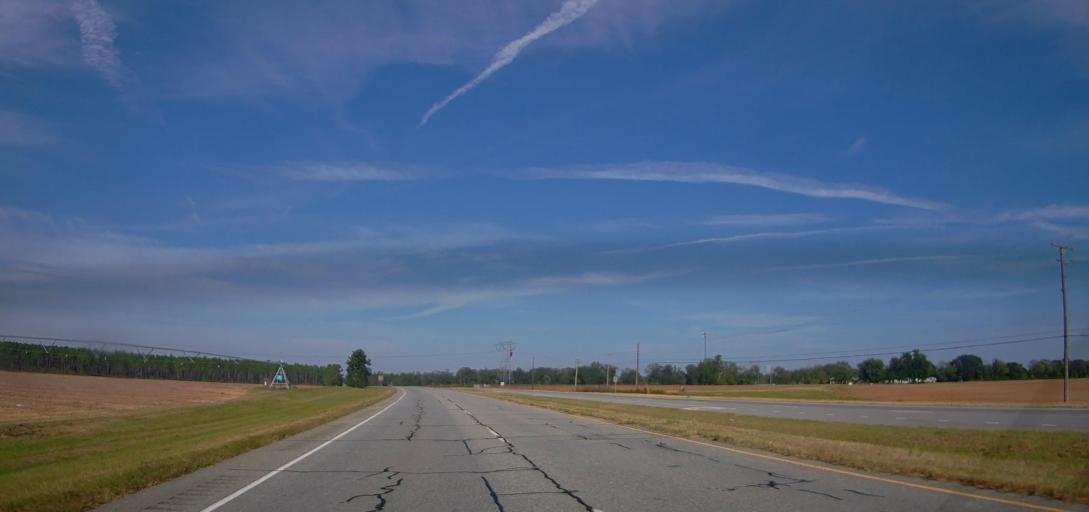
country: US
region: Georgia
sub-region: Dougherty County
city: Putney
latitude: 31.3605
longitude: -84.1559
